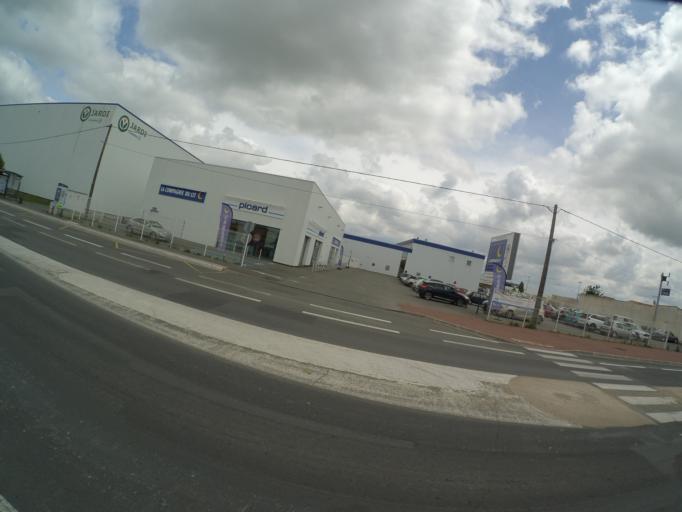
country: FR
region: Poitou-Charentes
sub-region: Departement de la Charente-Maritime
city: Rochefort
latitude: 45.9247
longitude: -0.9602
